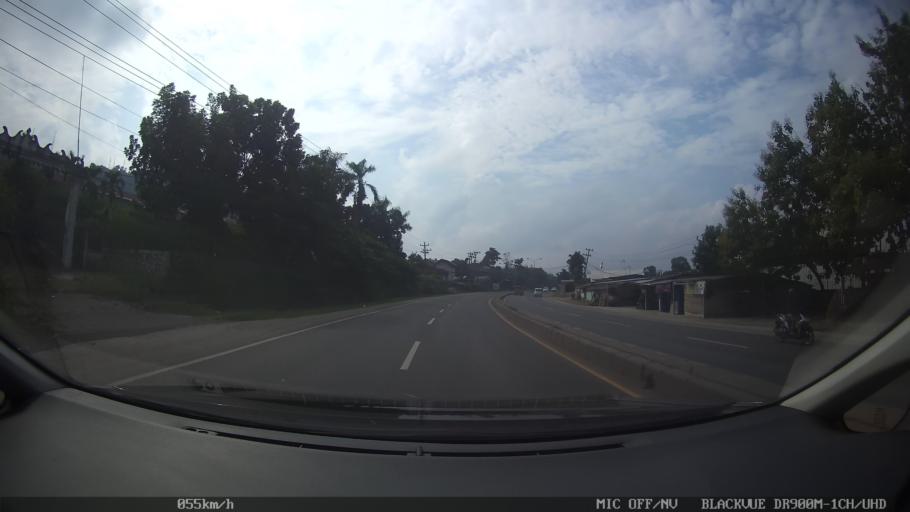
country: ID
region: Lampung
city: Bandarlampung
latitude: -5.4345
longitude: 105.2989
